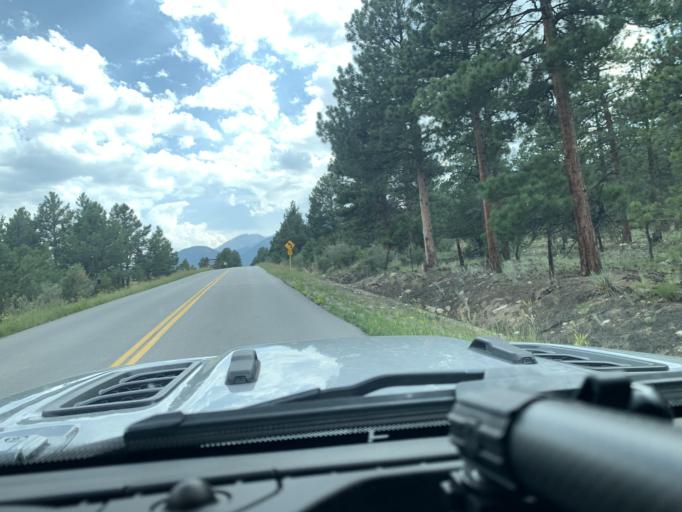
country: US
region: Colorado
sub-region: Chaffee County
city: Buena Vista
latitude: 38.7446
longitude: -106.1612
